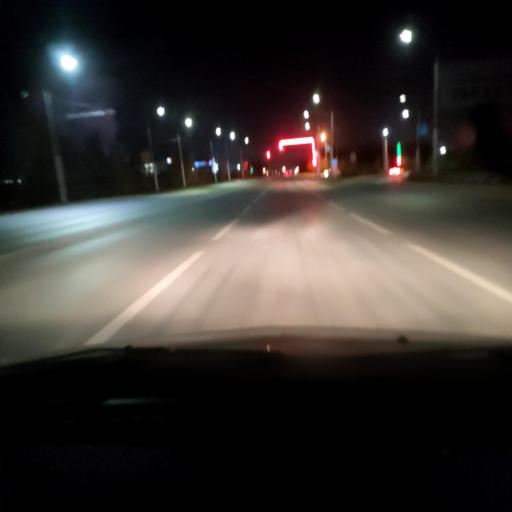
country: RU
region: Bashkortostan
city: Ufa
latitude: 54.7909
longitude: 56.0778
